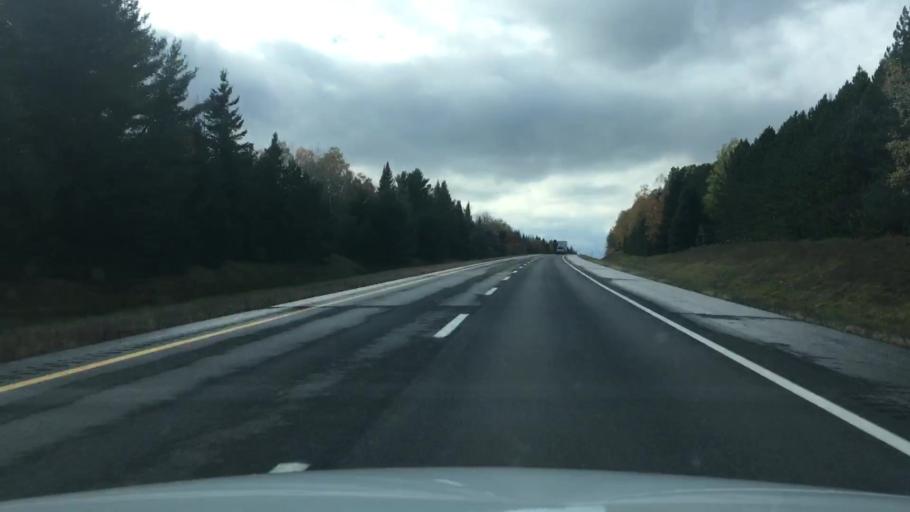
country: US
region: Maine
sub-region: Aroostook County
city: Hodgdon
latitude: 46.1406
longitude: -68.0151
